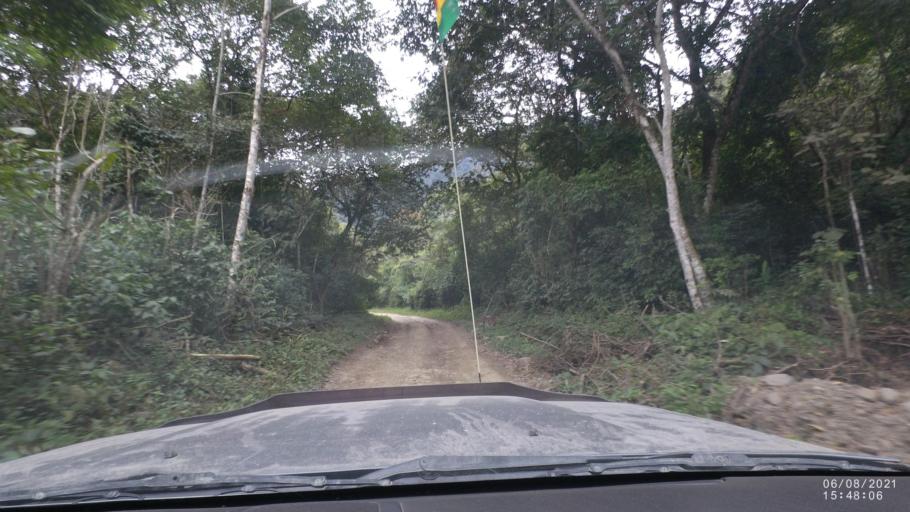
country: BO
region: La Paz
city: Quime
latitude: -16.5916
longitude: -66.7045
